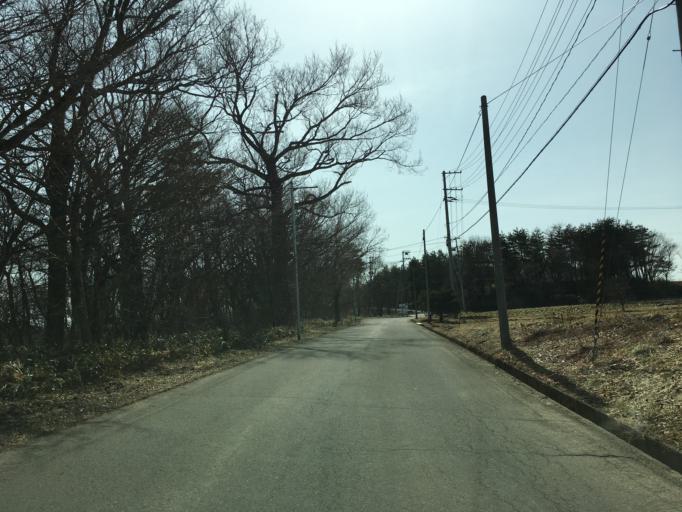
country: JP
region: Fukushima
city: Nihommatsu
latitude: 37.6351
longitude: 140.3592
